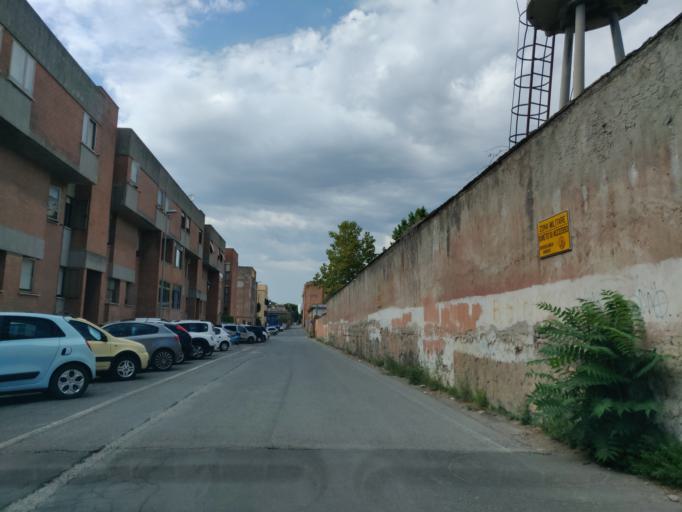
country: IT
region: Latium
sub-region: Citta metropolitana di Roma Capitale
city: Civitavecchia
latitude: 42.0878
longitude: 11.8093
